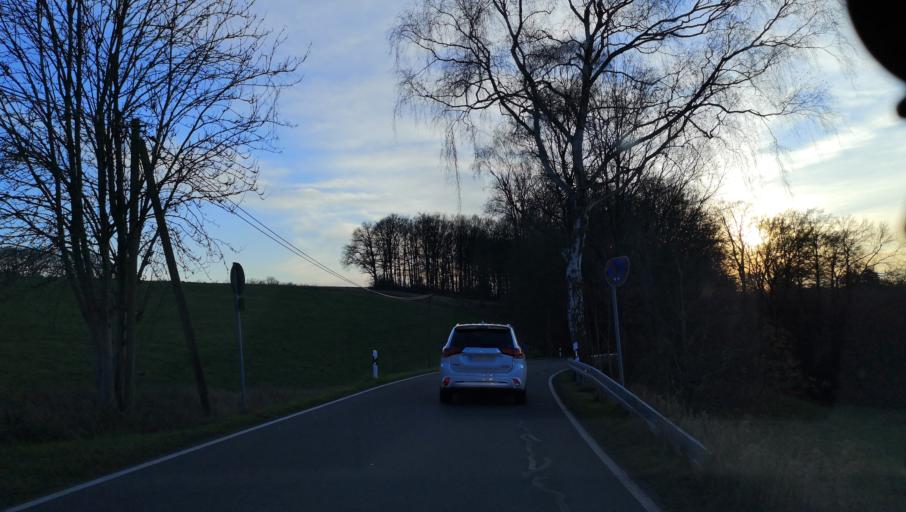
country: DE
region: North Rhine-Westphalia
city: Wipperfurth
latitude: 51.1507
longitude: 7.3900
